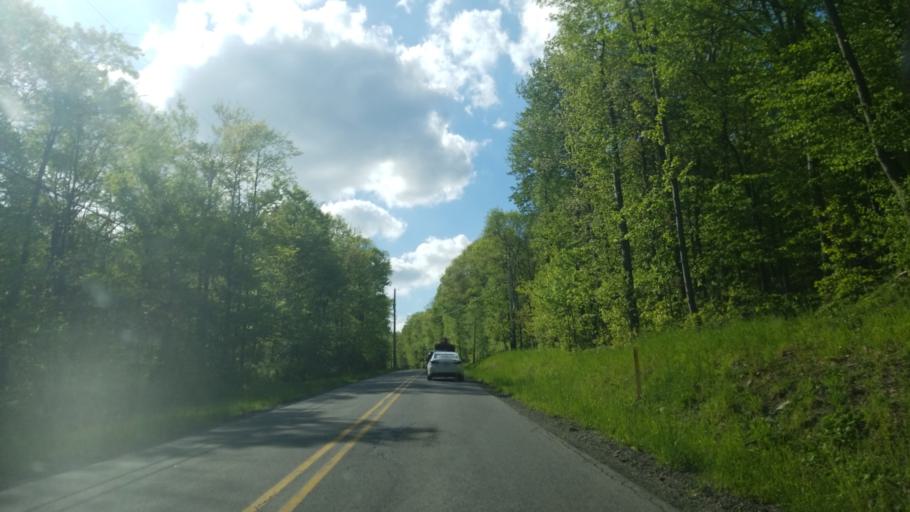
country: US
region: Pennsylvania
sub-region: Clearfield County
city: Osceola Mills
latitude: 40.9350
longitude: -78.3139
